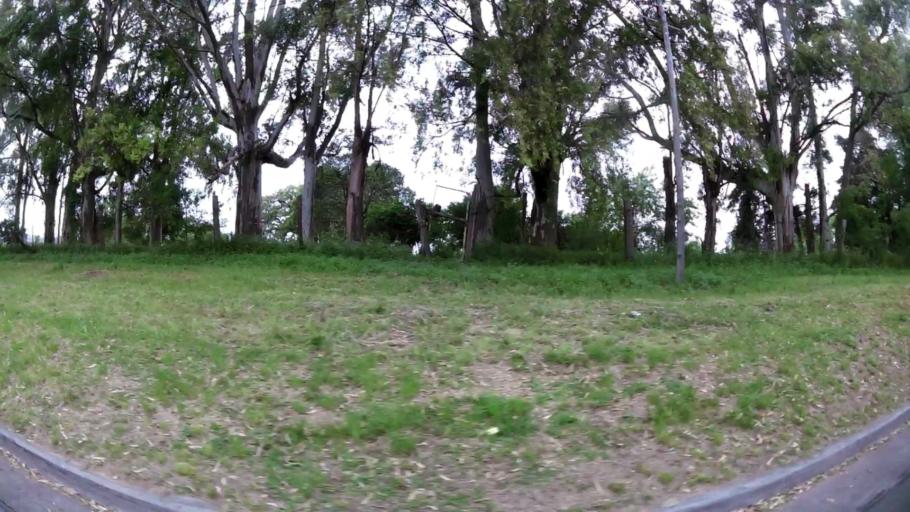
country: AR
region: Buenos Aires F.D.
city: Villa Lugano
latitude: -34.7292
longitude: -58.5152
